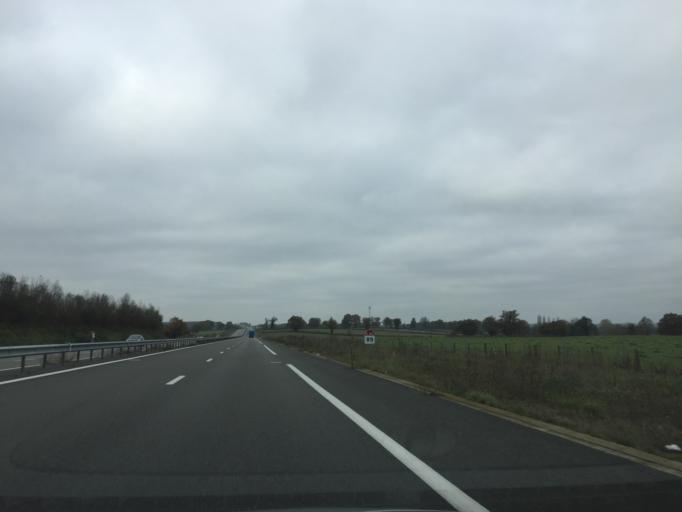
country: FR
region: Limousin
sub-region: Departement de la Creuse
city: Chambon-sur-Voueize
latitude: 46.2780
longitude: 2.3915
